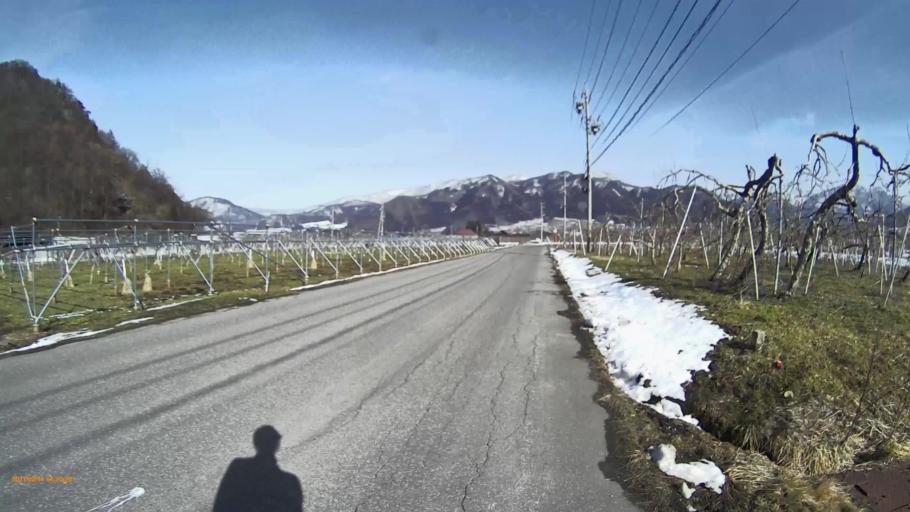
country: JP
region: Nagano
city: Nakano
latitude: 36.7461
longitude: 138.3922
